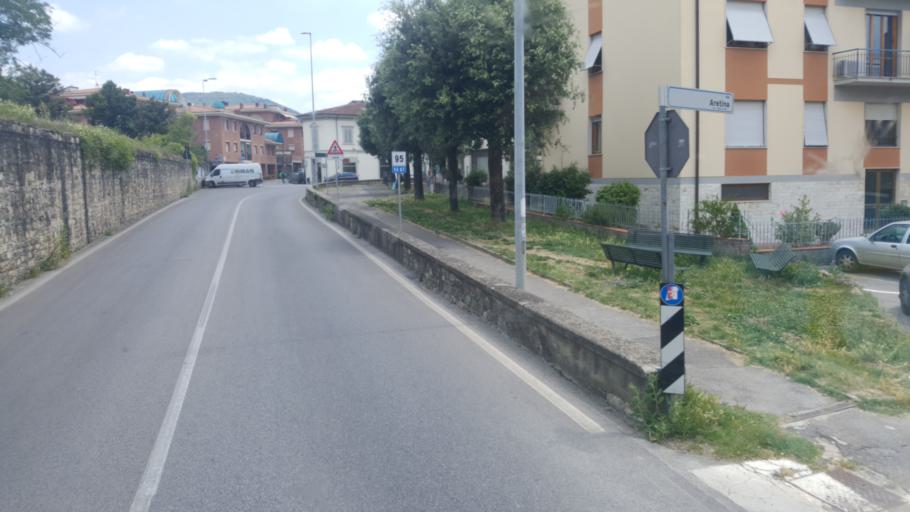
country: IT
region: Tuscany
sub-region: Province of Florence
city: Sieci
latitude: 43.7913
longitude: 11.3915
